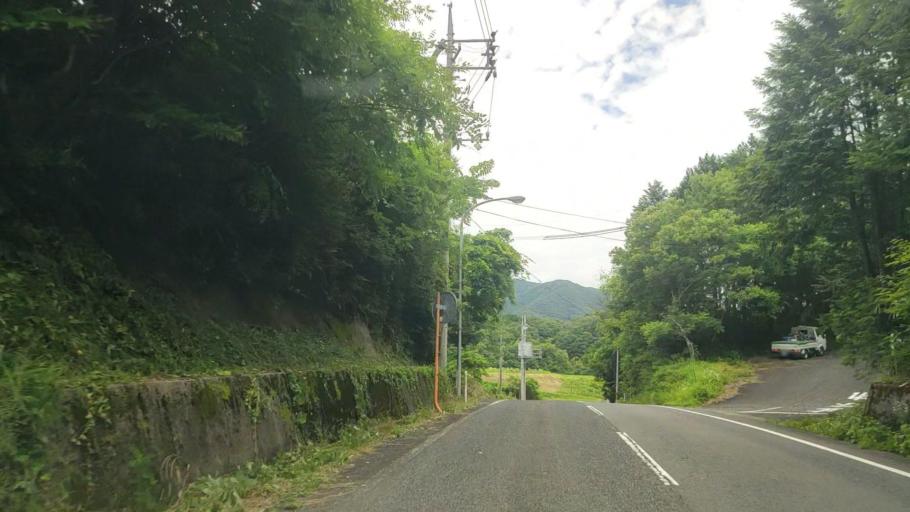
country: JP
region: Hyogo
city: Yamazakicho-nakabirose
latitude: 35.0951
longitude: 134.2895
